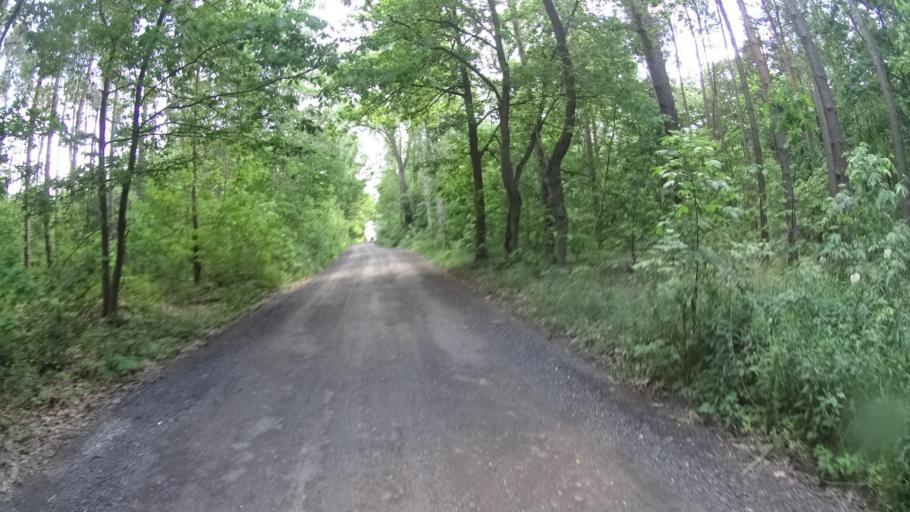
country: PL
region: Masovian Voivodeship
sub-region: Powiat pruszkowski
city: Nadarzyn
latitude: 52.0648
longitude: 20.8208
